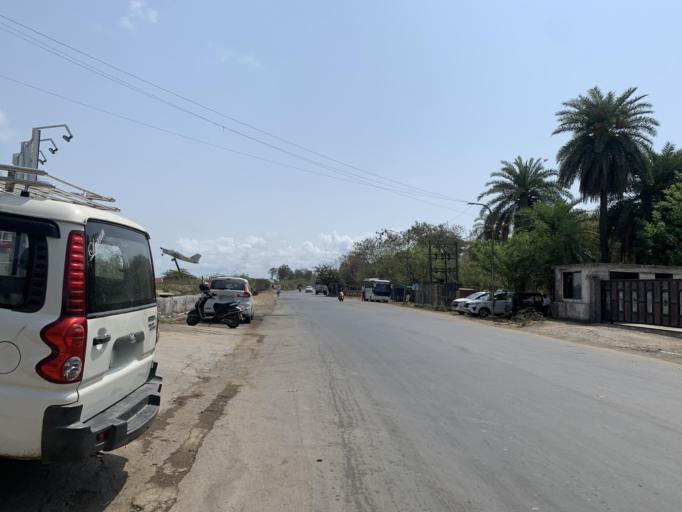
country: IN
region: Daman and Diu
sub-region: Daman District
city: Daman
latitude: 20.4541
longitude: 72.8398
